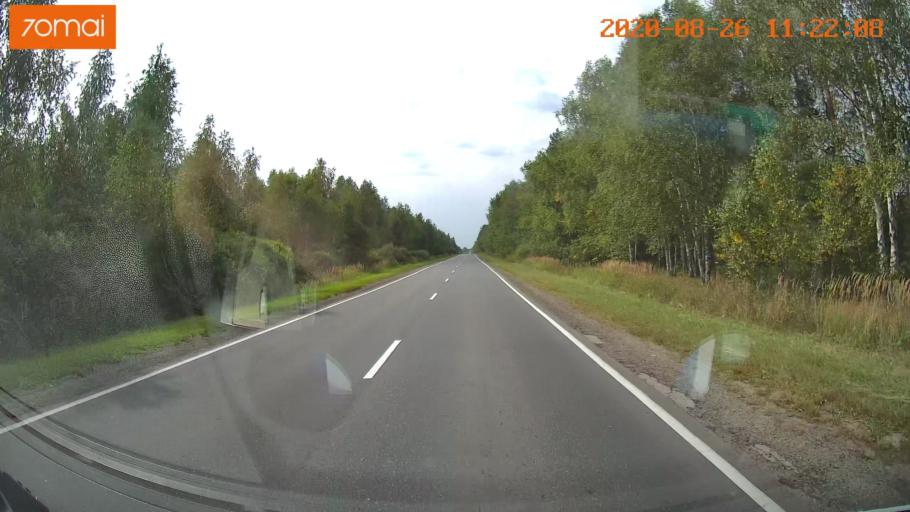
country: RU
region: Rjazan
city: Shilovo
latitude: 54.3676
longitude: 41.0325
